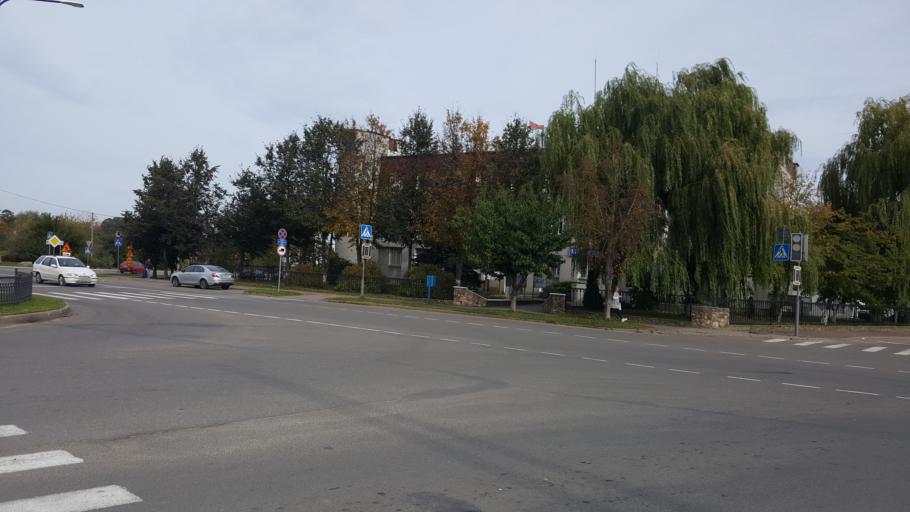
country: BY
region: Brest
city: Kamyanyets
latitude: 52.3973
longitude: 23.8274
